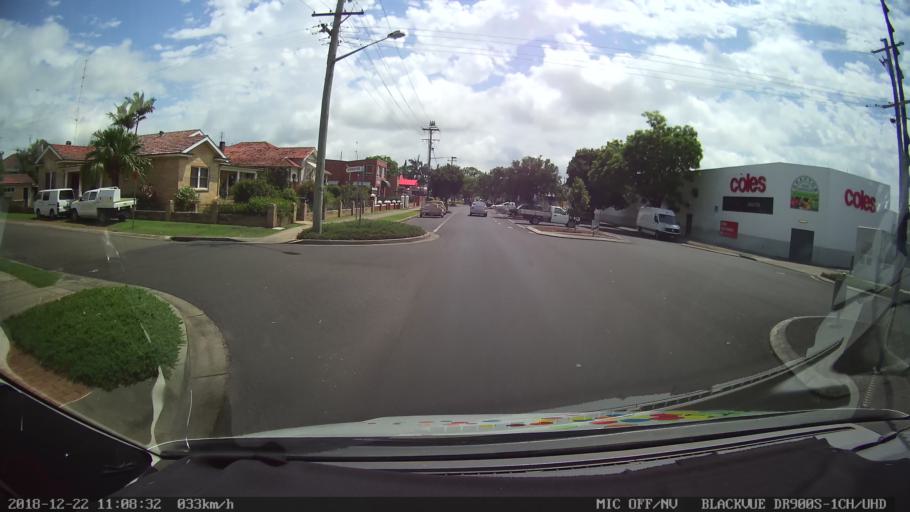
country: AU
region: New South Wales
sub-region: Clarence Valley
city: Grafton
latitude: -29.6889
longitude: 152.9316
